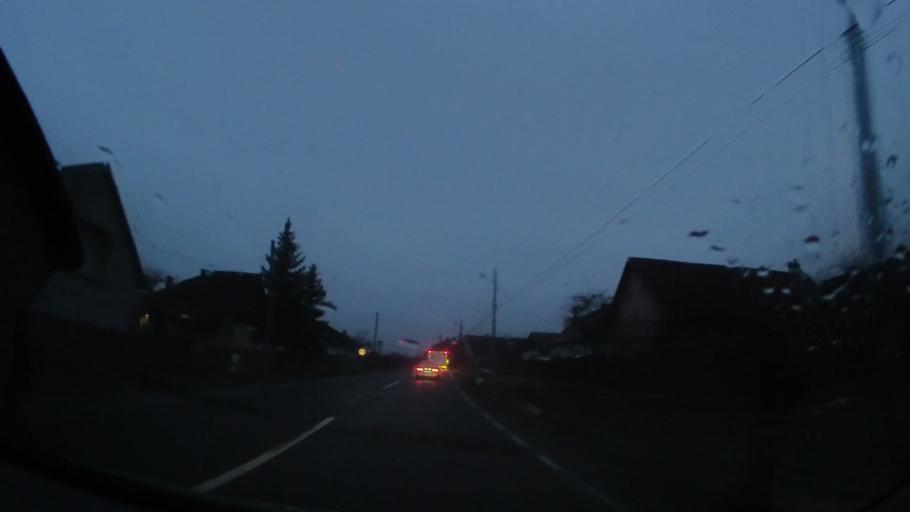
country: RO
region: Harghita
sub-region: Comuna Ditrau
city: Ditrau
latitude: 46.8117
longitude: 25.4940
